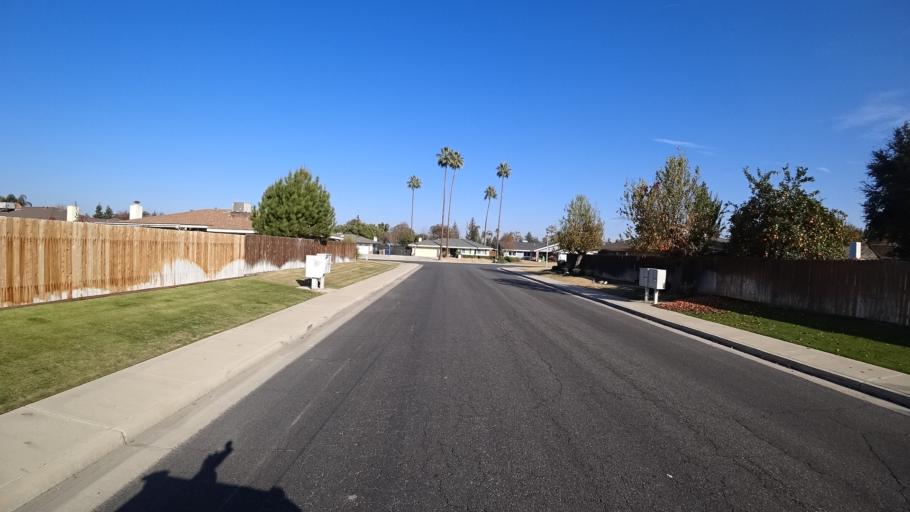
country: US
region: California
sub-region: Kern County
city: Greenacres
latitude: 35.3222
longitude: -119.1043
